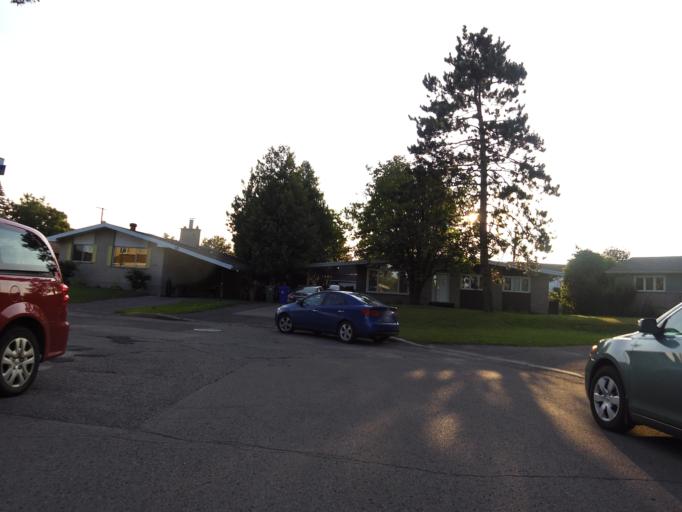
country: CA
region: Quebec
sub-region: Outaouais
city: Gatineau
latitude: 45.4665
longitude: -75.6936
